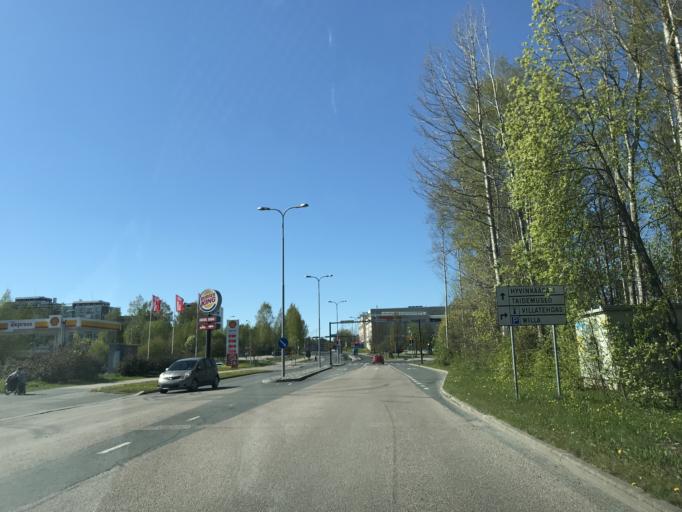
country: FI
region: Uusimaa
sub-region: Helsinki
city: Hyvinge
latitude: 60.6277
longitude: 24.8658
